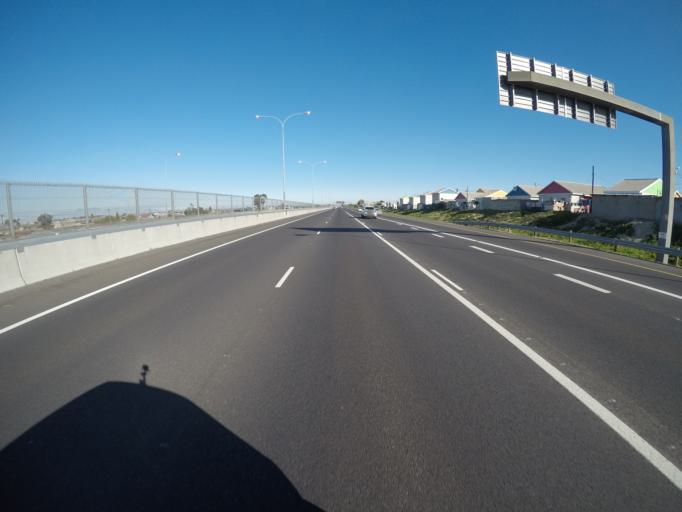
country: ZA
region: Western Cape
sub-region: City of Cape Town
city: Kraaifontein
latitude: -33.9600
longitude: 18.6562
